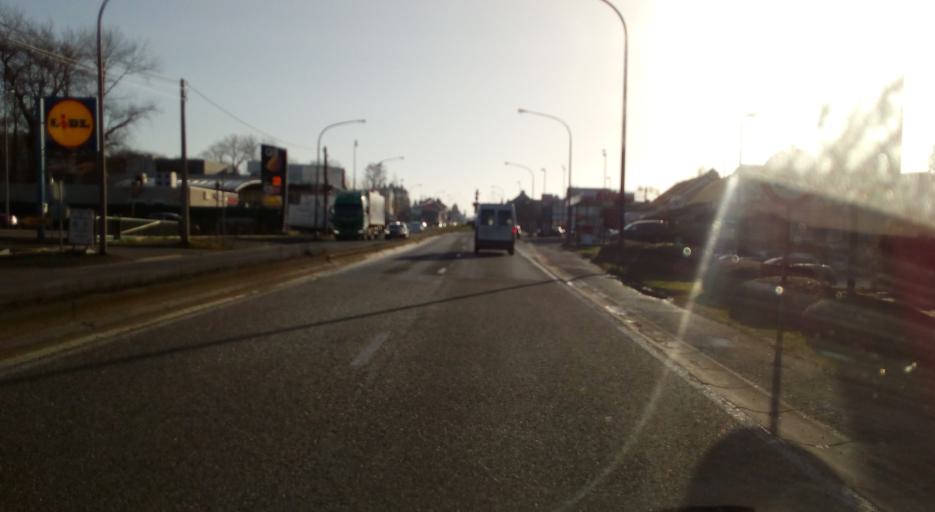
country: BE
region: Wallonia
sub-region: Province du Hainaut
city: Gerpinnes
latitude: 50.3447
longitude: 4.4730
